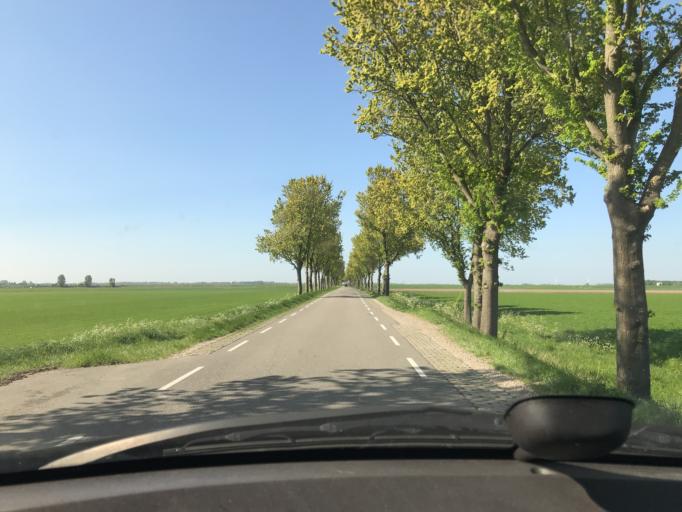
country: NL
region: Zeeland
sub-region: Gemeente Goes
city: Goes
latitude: 51.5312
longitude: 3.8538
